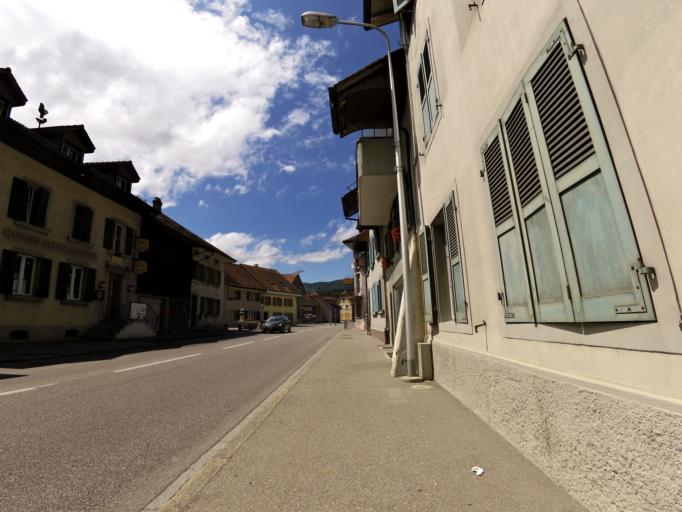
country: CH
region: Solothurn
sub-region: Bezirk Thal
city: Balsthal
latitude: 47.3069
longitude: 7.6900
